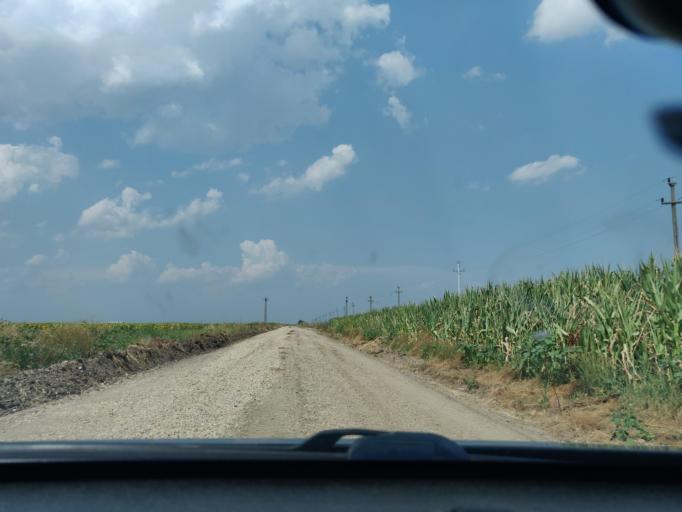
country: RO
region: Teleorman
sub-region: Comuna Sarbeni
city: Sarbeni
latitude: 44.4940
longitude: 25.3945
